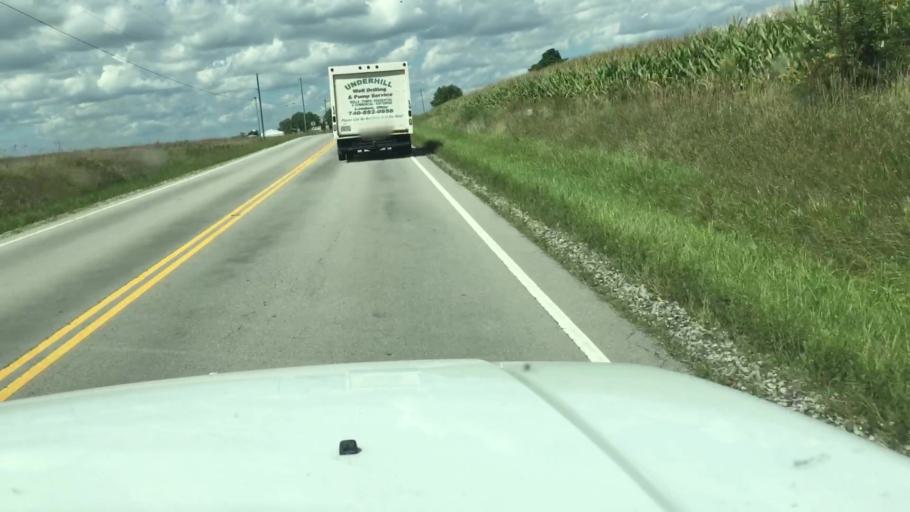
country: US
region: Ohio
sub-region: Madison County
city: Bethel
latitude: 39.8179
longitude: -83.3556
